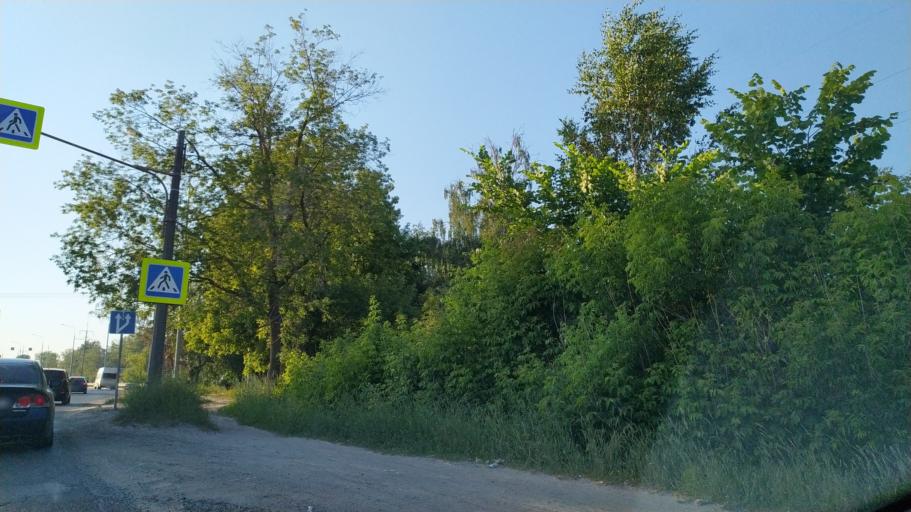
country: RU
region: Chuvashia
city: Kugesi
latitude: 56.0744
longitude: 47.2771
